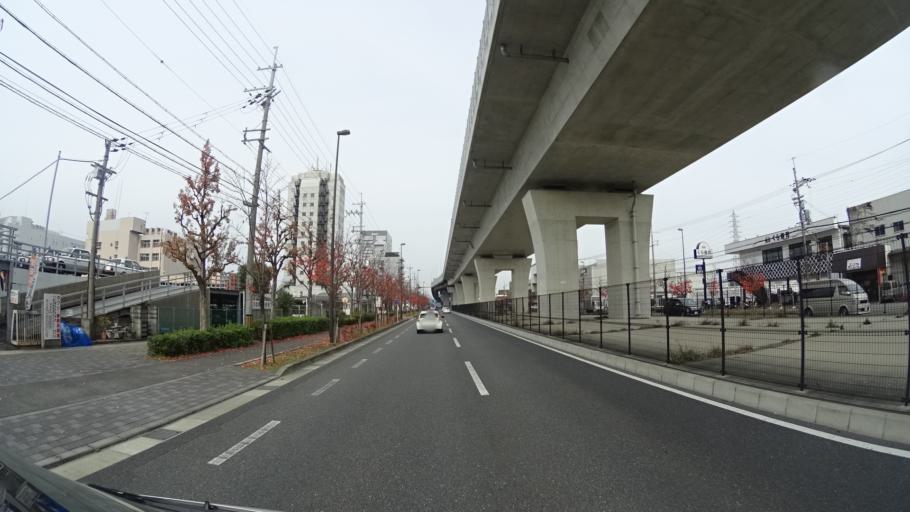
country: JP
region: Kyoto
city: Muko
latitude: 34.9416
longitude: 135.7515
